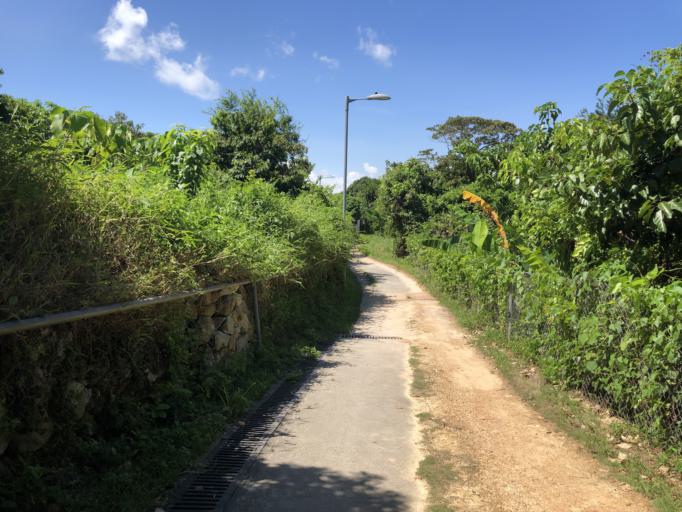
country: HK
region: Tuen Mun
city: Tuen Mun
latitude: 22.2895
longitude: 113.9787
